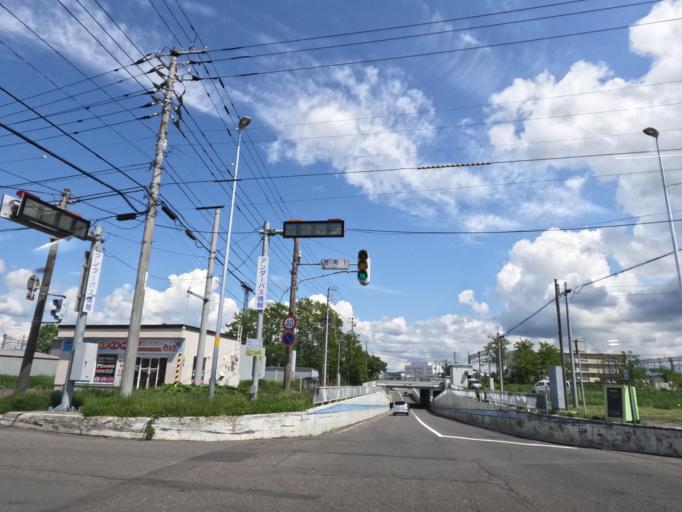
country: JP
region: Hokkaido
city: Takikawa
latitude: 43.5596
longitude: 141.9013
